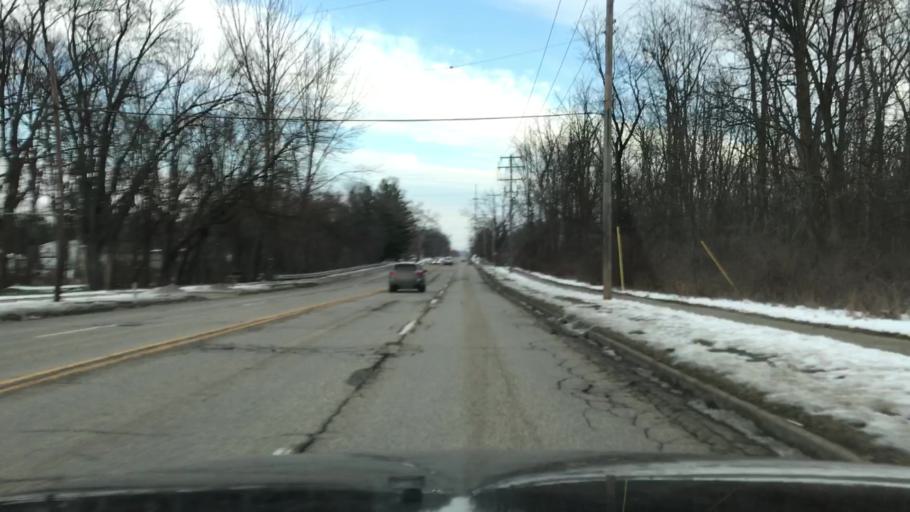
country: US
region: Michigan
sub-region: Kent County
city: Grandville
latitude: 42.9006
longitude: -85.7438
